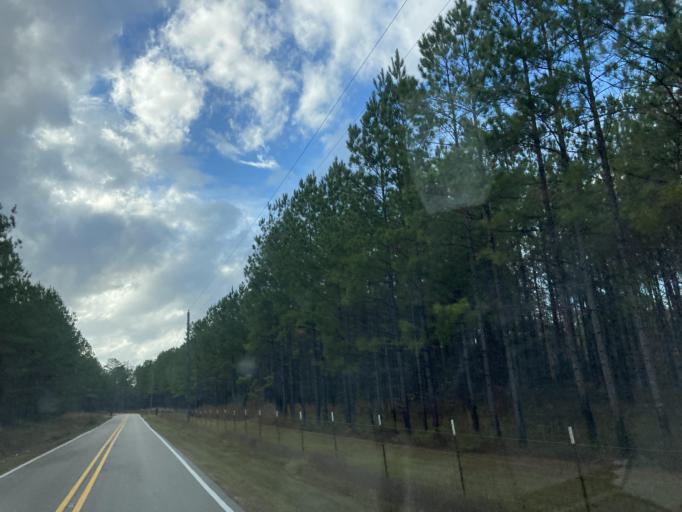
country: US
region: Mississippi
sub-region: Lamar County
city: Purvis
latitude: 31.1630
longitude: -89.5950
